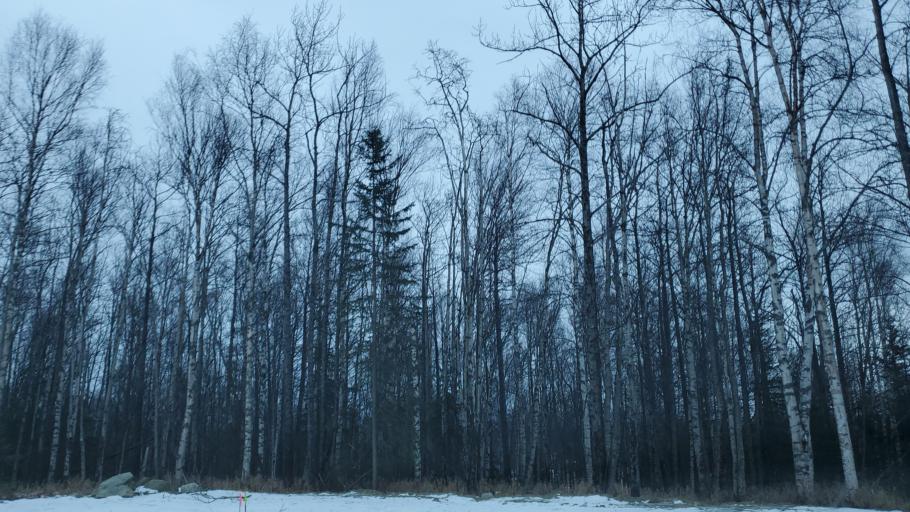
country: US
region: Alaska
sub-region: Matanuska-Susitna Borough
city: Gateway
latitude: 61.6555
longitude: -149.2279
